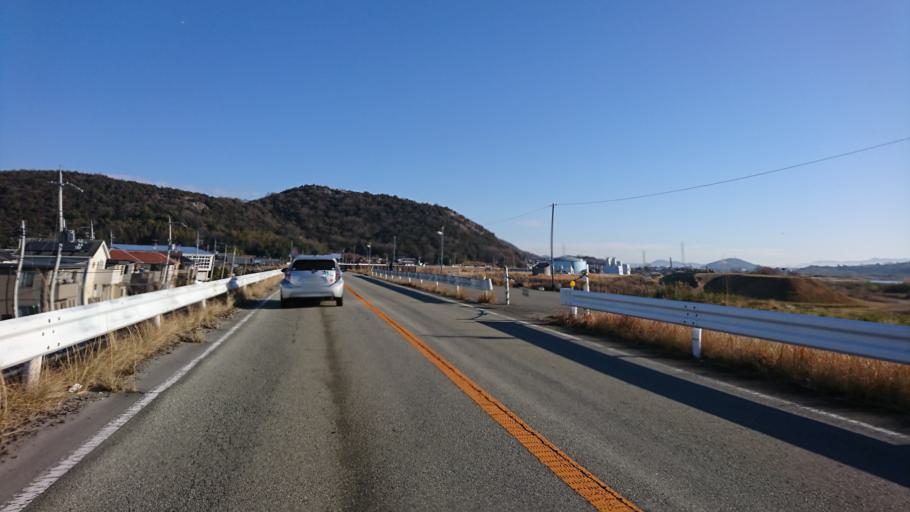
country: JP
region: Hyogo
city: Kakogawacho-honmachi
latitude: 34.7831
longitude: 134.8453
